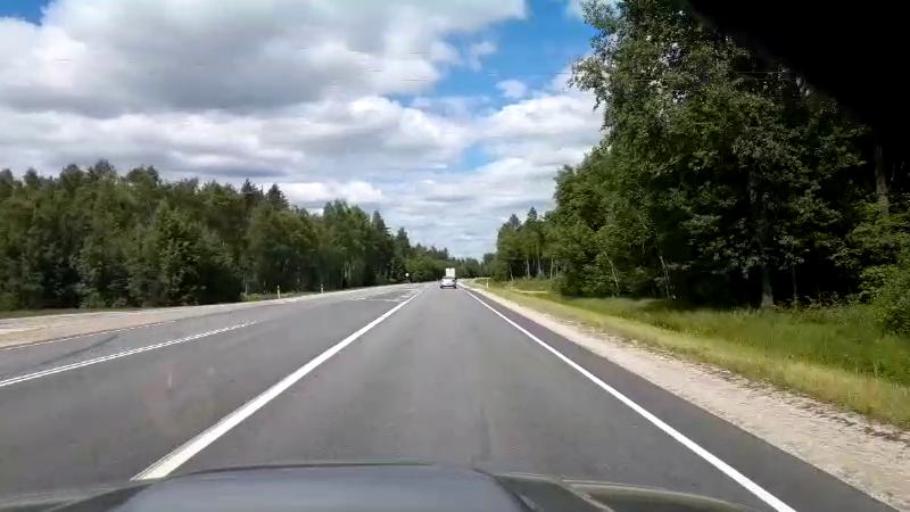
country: EE
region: Paernumaa
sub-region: Halinga vald
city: Parnu-Jaagupi
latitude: 58.7085
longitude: 24.4240
